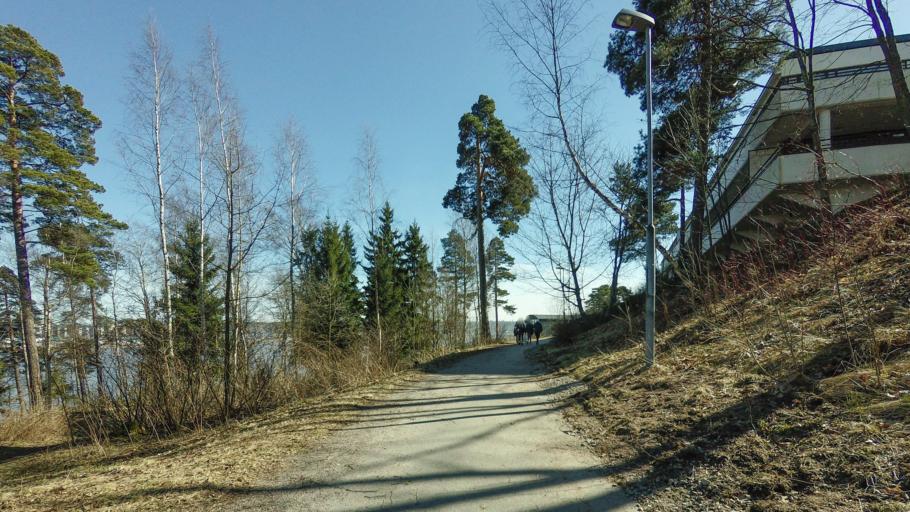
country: FI
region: Uusimaa
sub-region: Helsinki
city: Helsinki
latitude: 60.1877
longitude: 25.0175
